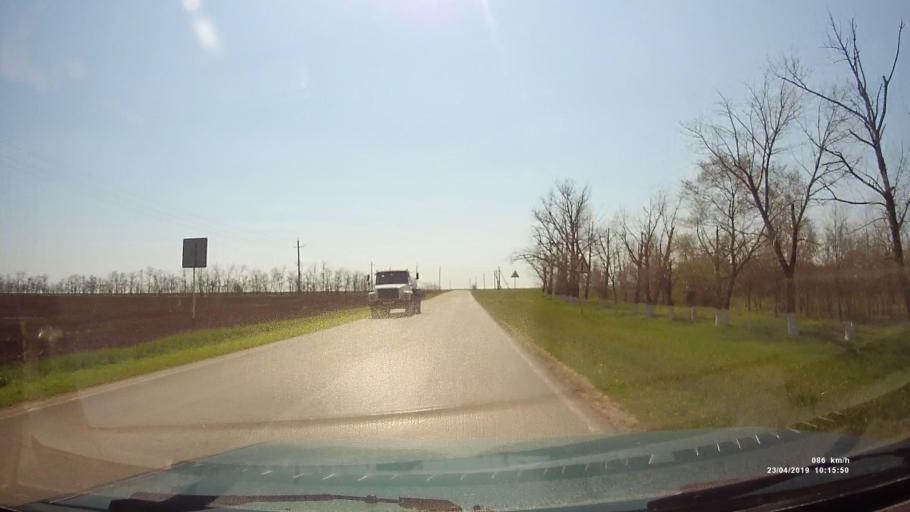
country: RU
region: Rostov
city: Sovetskoye
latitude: 46.6632
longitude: 42.3855
